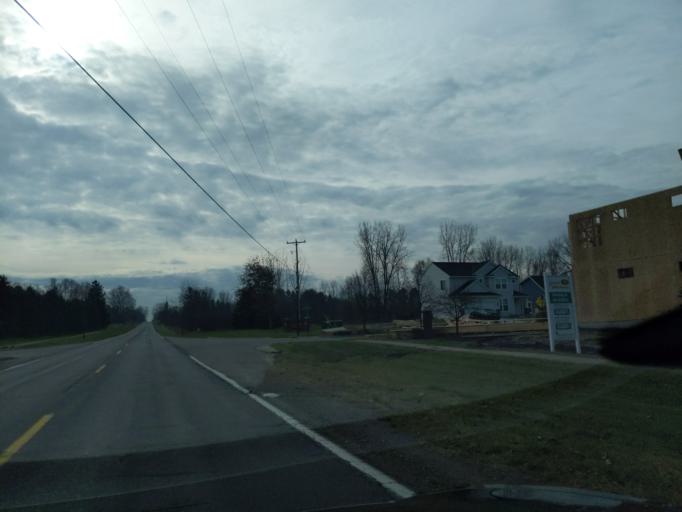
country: US
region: Michigan
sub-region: Ingham County
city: Holt
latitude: 42.6234
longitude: -84.5232
